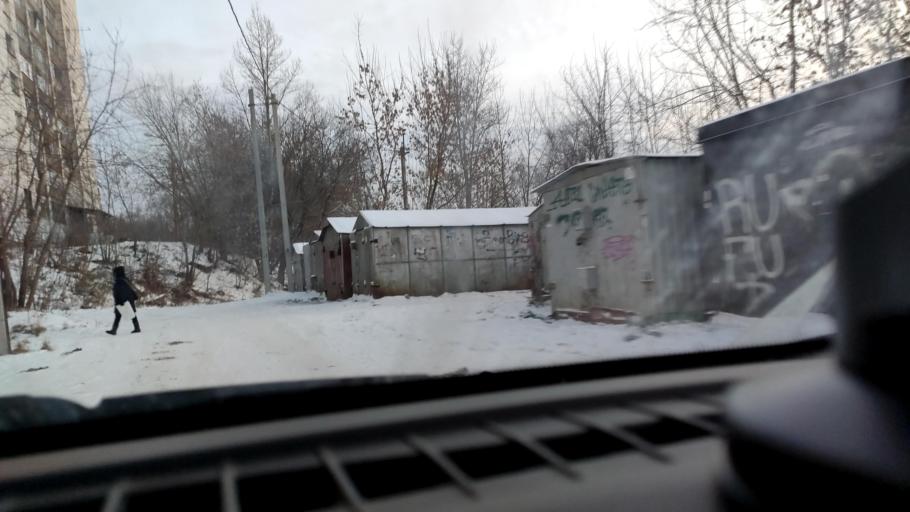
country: RU
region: Perm
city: Perm
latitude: 58.0239
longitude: 56.3062
